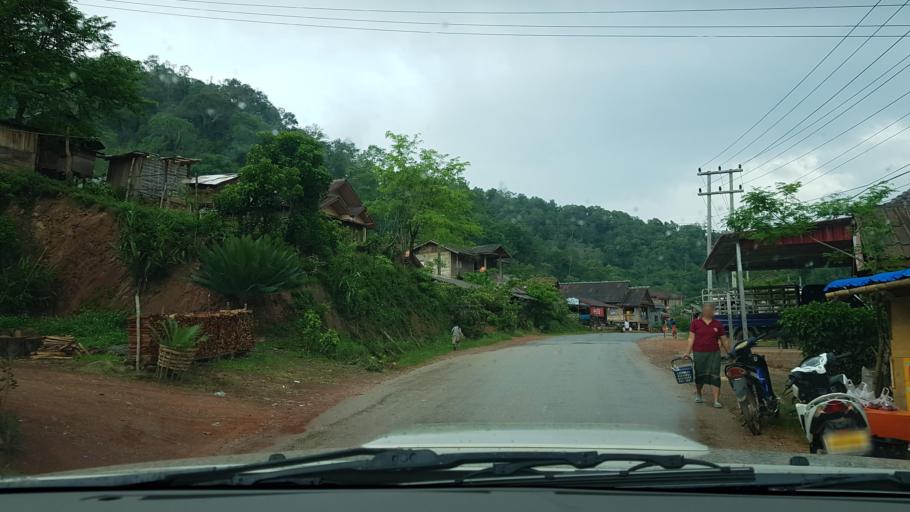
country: LA
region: Oudomxai
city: Muang Xay
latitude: 20.5918
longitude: 101.9338
